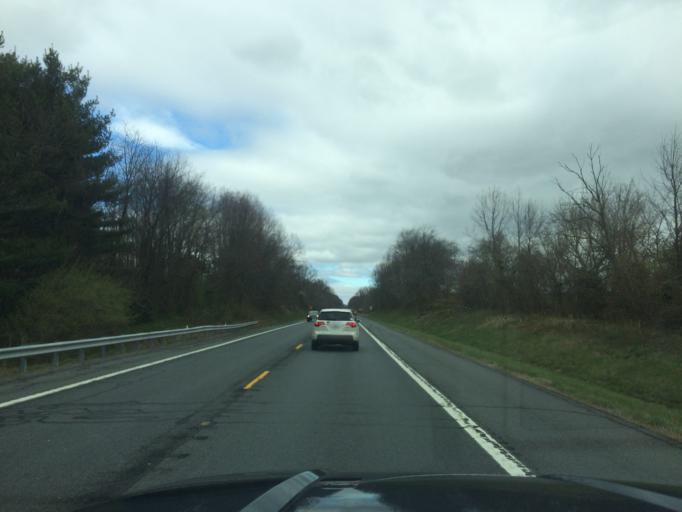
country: US
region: Maryland
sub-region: Frederick County
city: Jefferson
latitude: 39.3313
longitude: -77.5100
